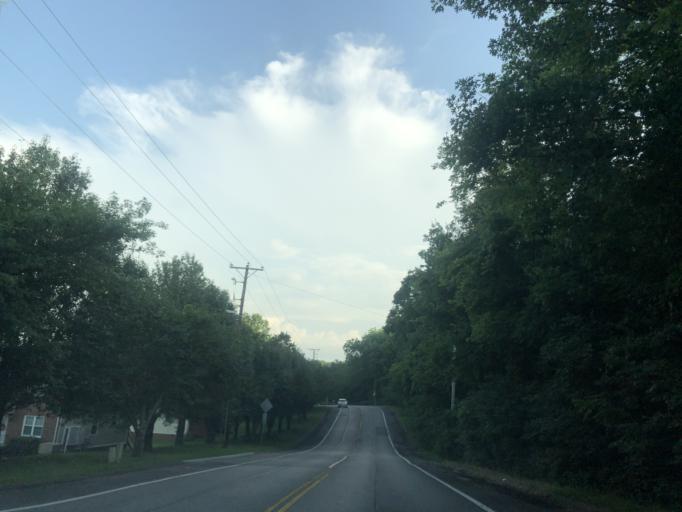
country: US
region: Tennessee
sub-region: Davidson County
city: Lakewood
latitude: 36.1386
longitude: -86.6411
